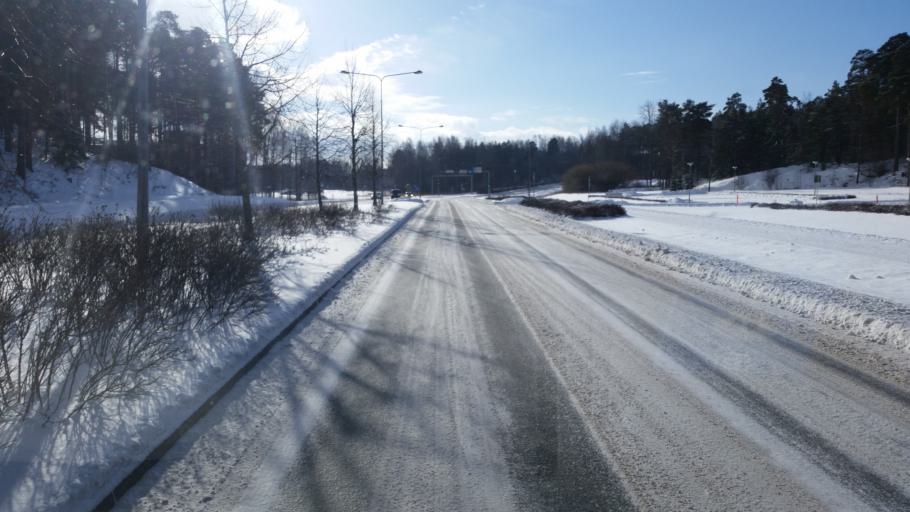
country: FI
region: Varsinais-Suomi
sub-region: Turku
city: Turku
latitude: 60.4326
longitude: 22.3178
